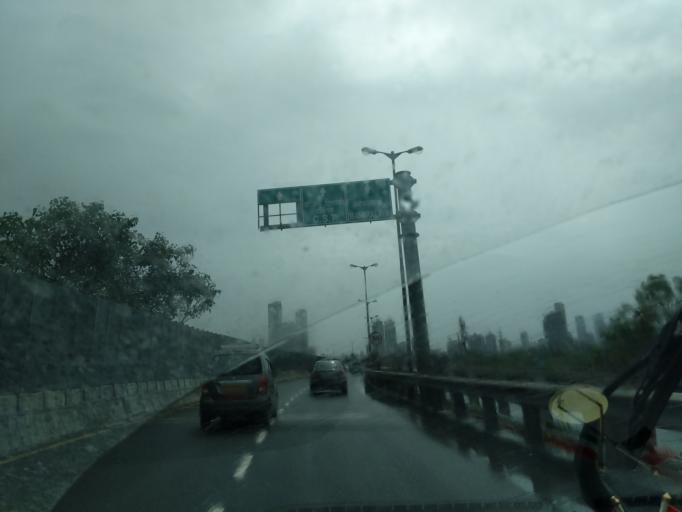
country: IN
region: Maharashtra
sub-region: Mumbai Suburban
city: Mumbai
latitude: 19.0109
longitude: 72.8680
